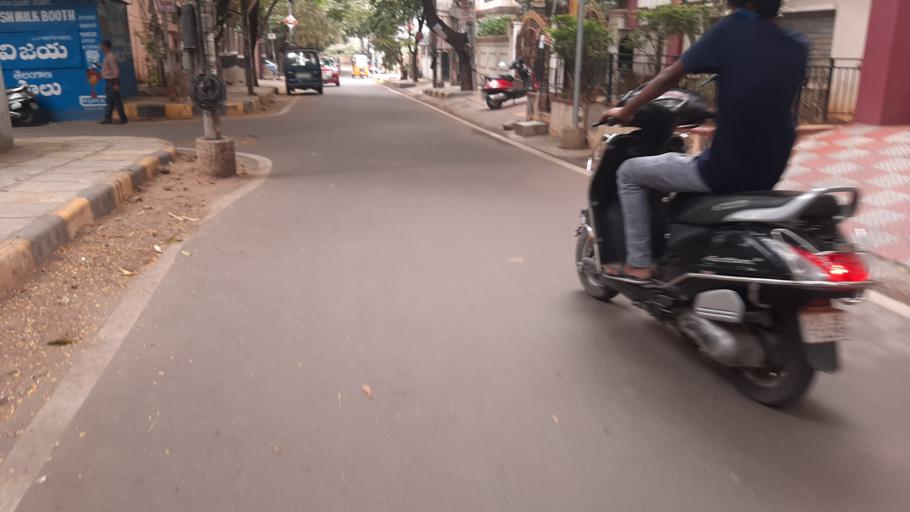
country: IN
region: Telangana
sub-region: Rangareddi
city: Kukatpalli
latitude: 17.4438
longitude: 78.4448
